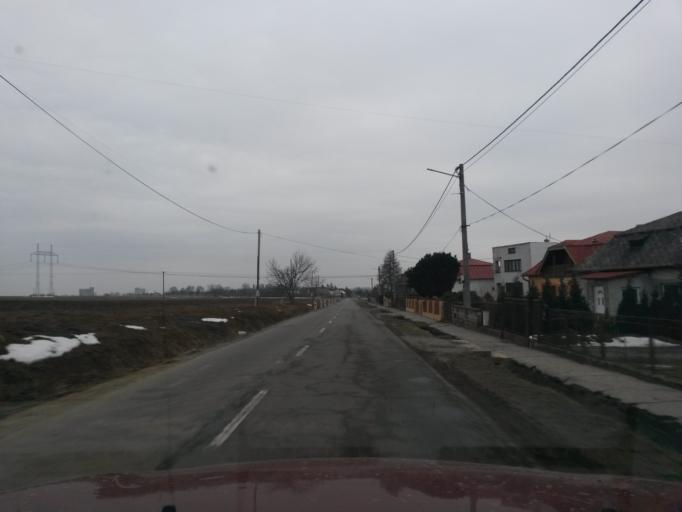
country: SK
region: Kosicky
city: Trebisov
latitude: 48.6930
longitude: 21.8094
